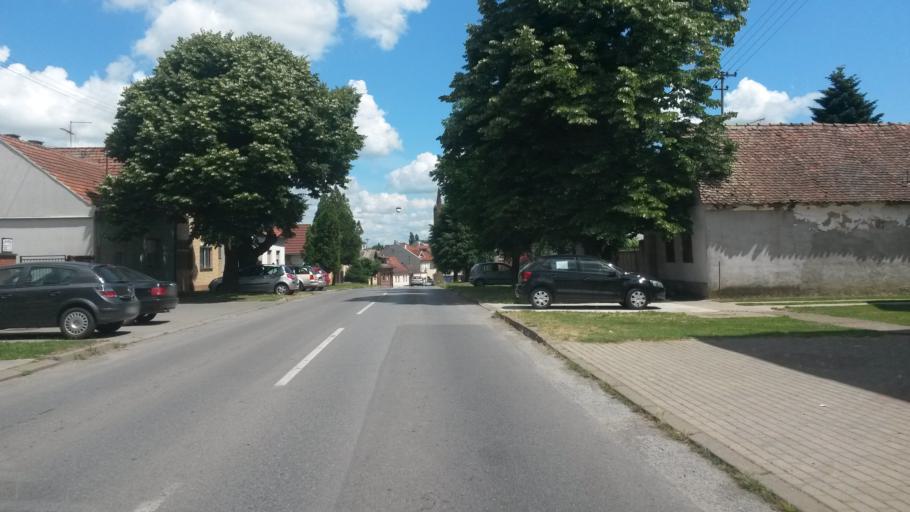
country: HR
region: Osjecko-Baranjska
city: Piskorevci
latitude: 45.3102
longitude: 18.4017
